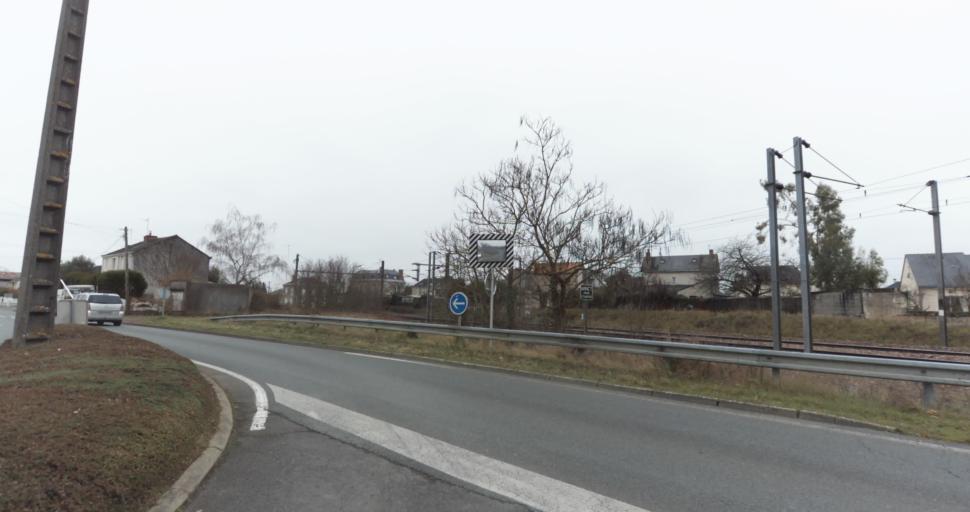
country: FR
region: Pays de la Loire
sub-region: Departement de Maine-et-Loire
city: Montreuil-Bellay
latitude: 47.1269
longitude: -0.1491
